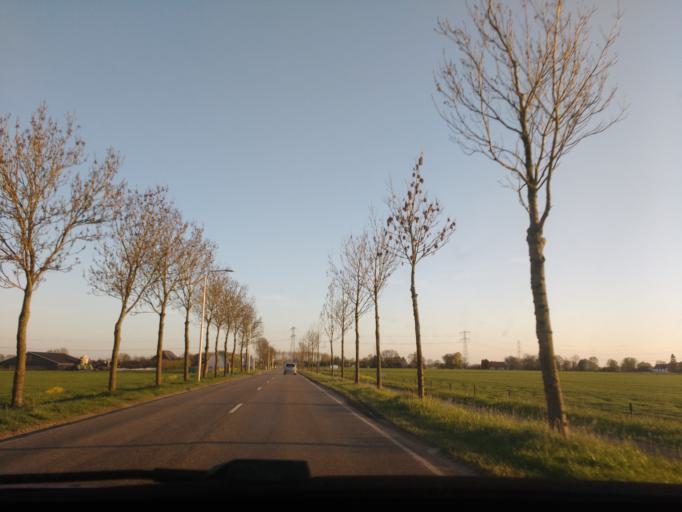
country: NL
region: Gelderland
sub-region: Gemeente Overbetuwe
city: Elst
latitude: 51.9022
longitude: 5.8377
